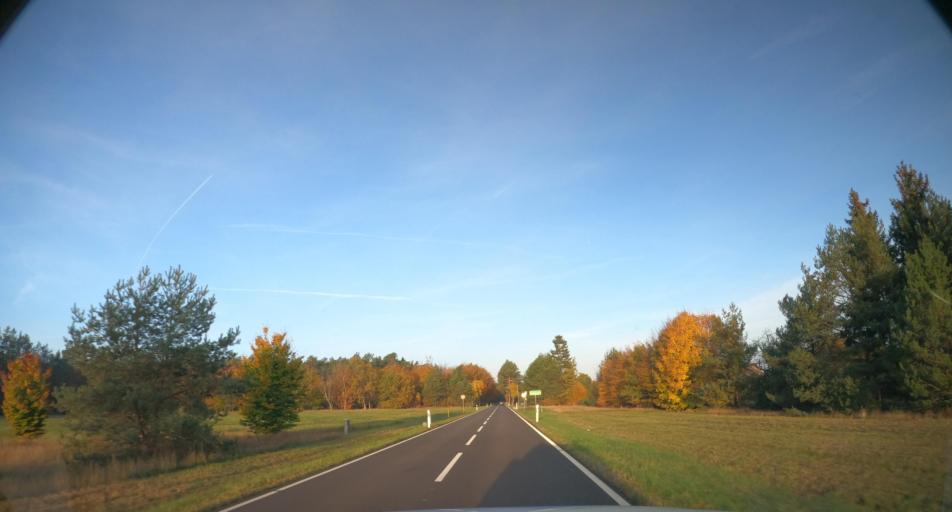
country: DE
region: Mecklenburg-Vorpommern
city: Ahlbeck
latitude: 53.6223
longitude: 14.2352
